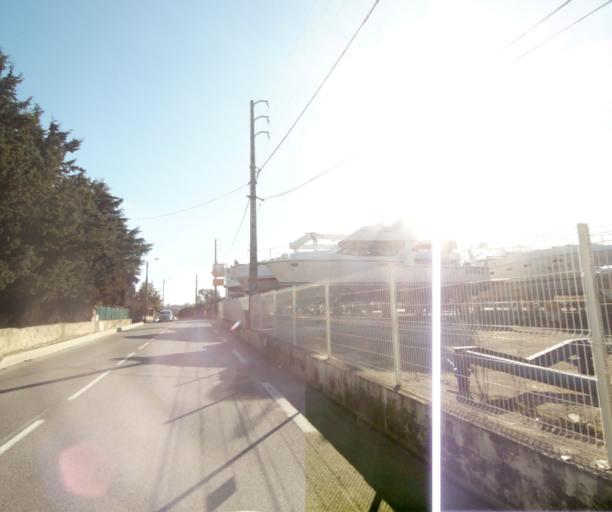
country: FR
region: Provence-Alpes-Cote d'Azur
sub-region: Departement des Alpes-Maritimes
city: Biot
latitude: 43.6050
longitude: 7.1123
